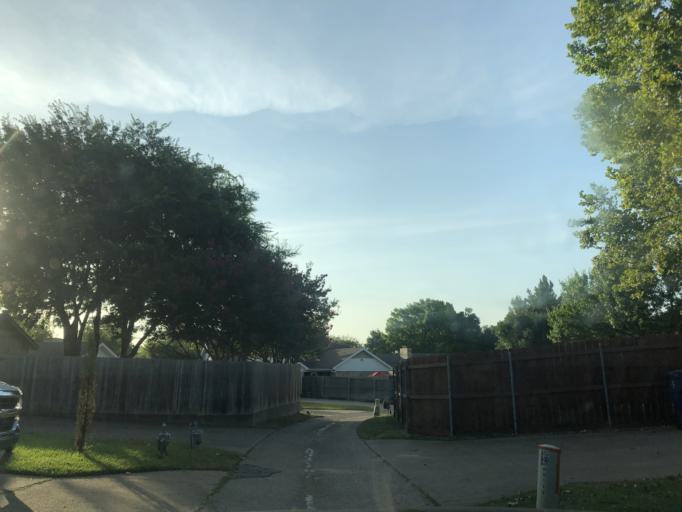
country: US
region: Texas
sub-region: Dallas County
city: Garland
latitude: 32.8563
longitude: -96.6249
